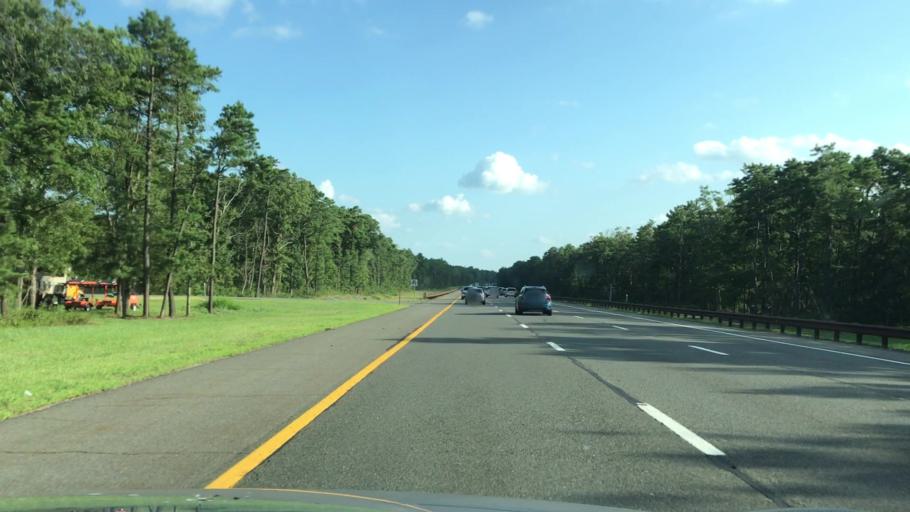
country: US
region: New Jersey
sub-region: Ocean County
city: Forked River
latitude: 39.8474
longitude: -74.2243
